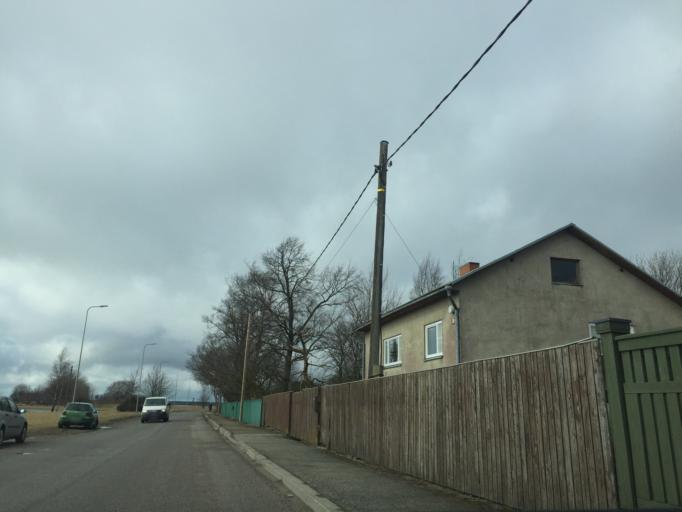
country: EE
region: Laeaene
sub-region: Haapsalu linn
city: Haapsalu
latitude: 58.9530
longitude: 23.5242
